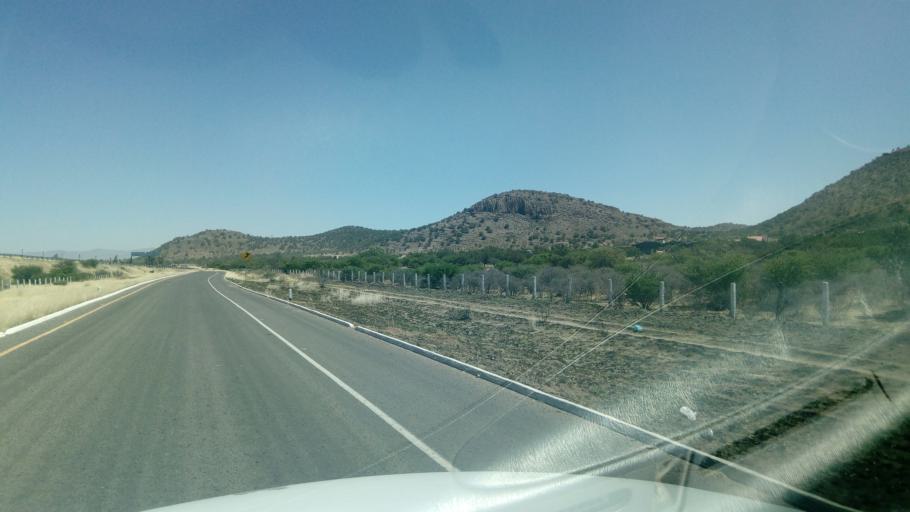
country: MX
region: Durango
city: Victoria de Durango
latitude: 24.1526
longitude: -104.7075
